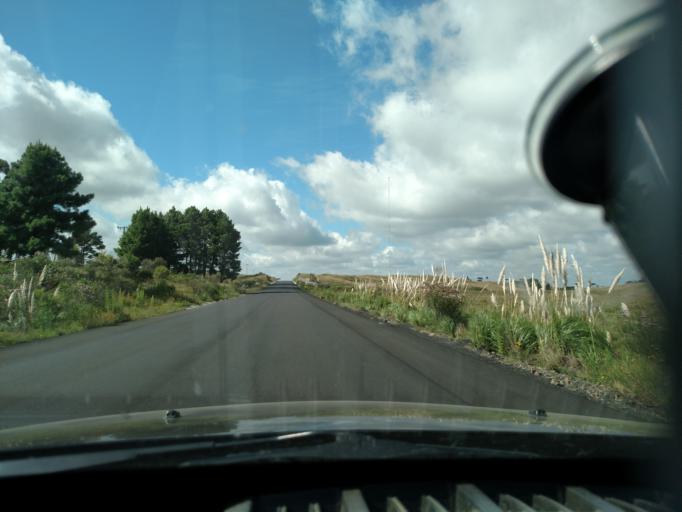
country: BR
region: Santa Catarina
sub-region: Lages
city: Lages
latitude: -27.9856
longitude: -50.0909
